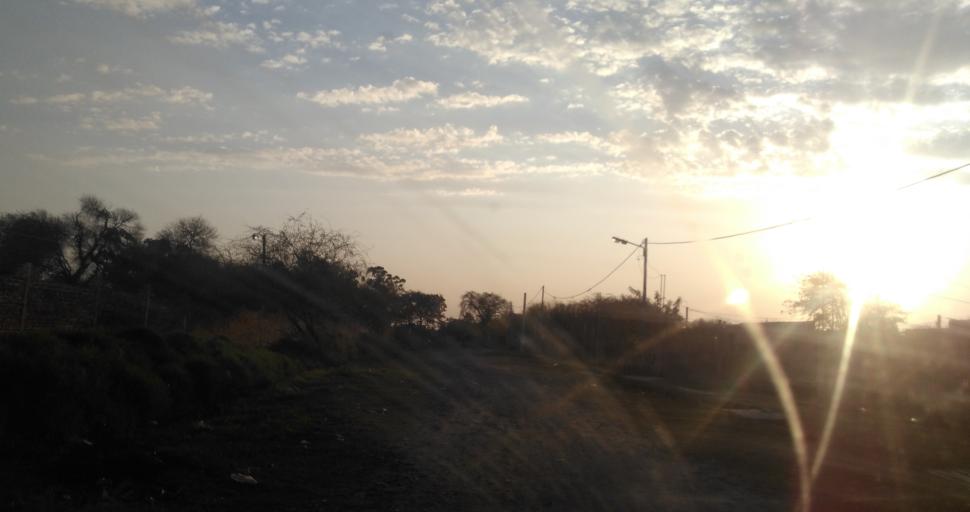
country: AR
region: Chaco
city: Fontana
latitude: -27.4630
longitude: -59.0359
